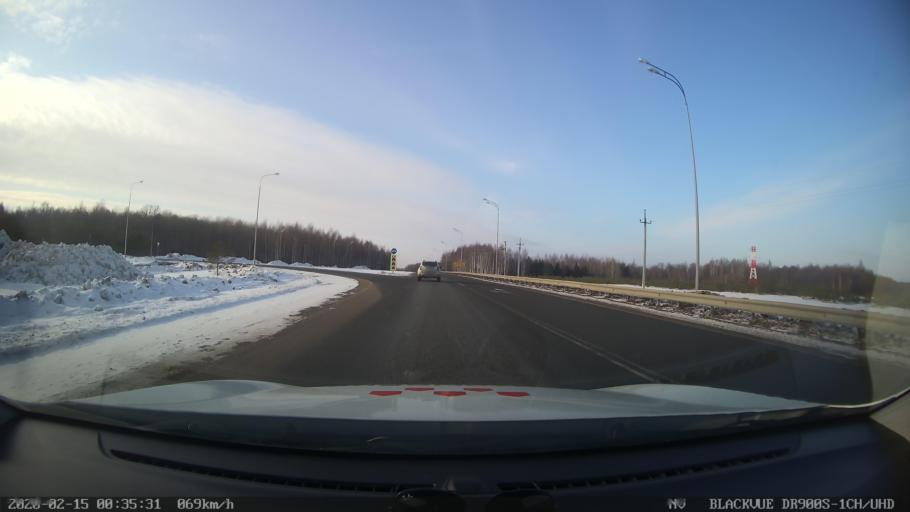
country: RU
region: Tatarstan
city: Verkhniy Uslon
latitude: 55.7089
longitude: 48.8908
